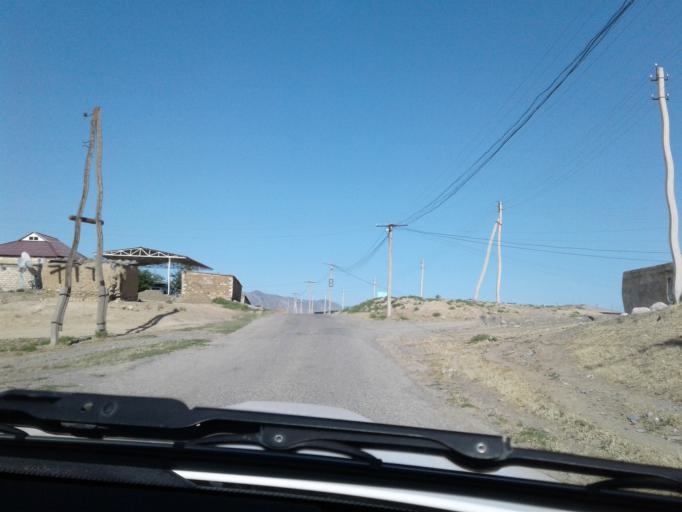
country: TM
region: Balkan
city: Magtymguly
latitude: 38.6826
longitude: 56.4604
